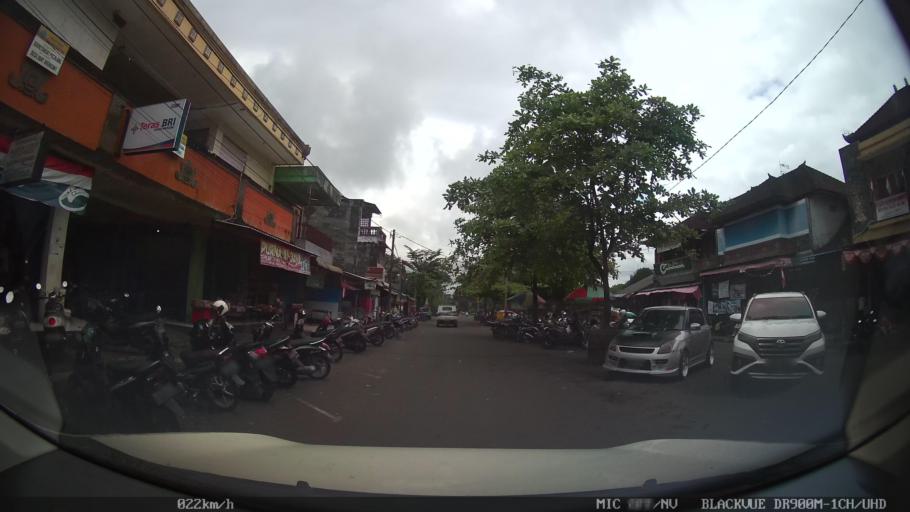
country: ID
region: Bali
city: Banjar Serangan
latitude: -8.5437
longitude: 115.1687
